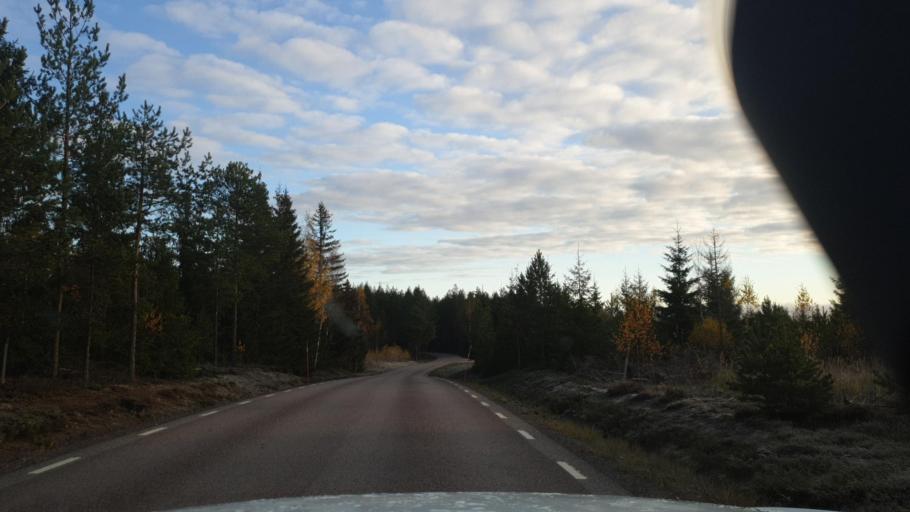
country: SE
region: Vaermland
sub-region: Eda Kommun
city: Charlottenberg
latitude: 59.7934
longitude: 12.2306
